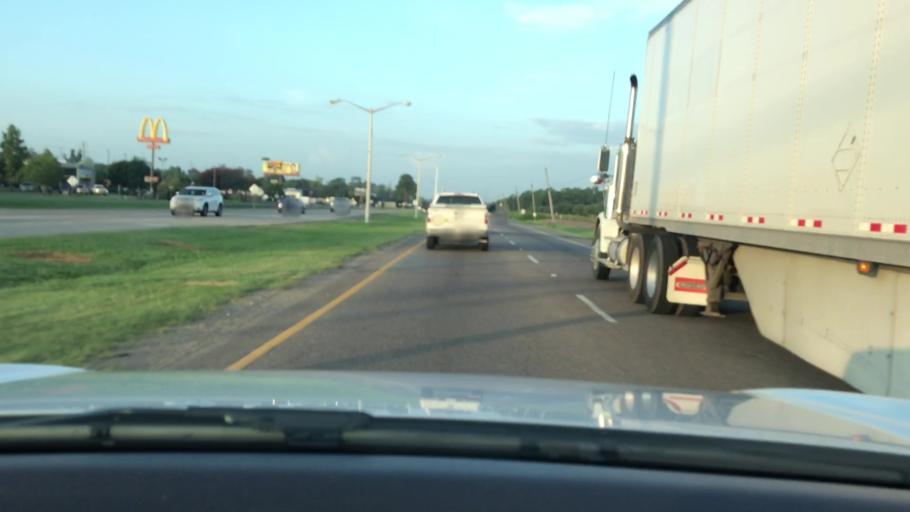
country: US
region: Louisiana
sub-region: West Baton Rouge Parish
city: Brusly
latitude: 30.3864
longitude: -91.2452
